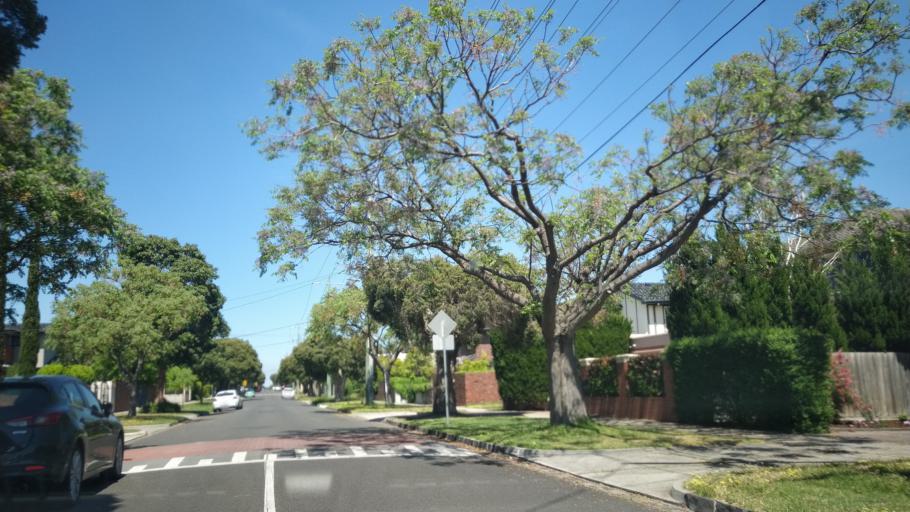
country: AU
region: Victoria
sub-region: Glen Eira
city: Caulfield South
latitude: -37.8928
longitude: 145.0324
